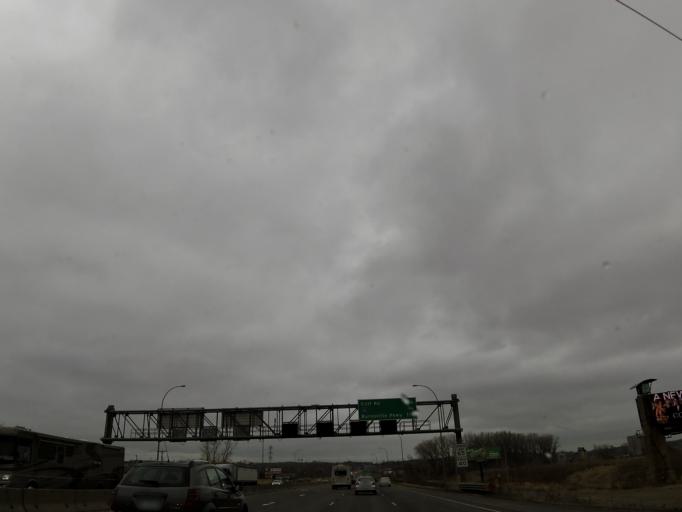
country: US
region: Minnesota
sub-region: Dakota County
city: Burnsville
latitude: 44.7907
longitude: -93.2890
